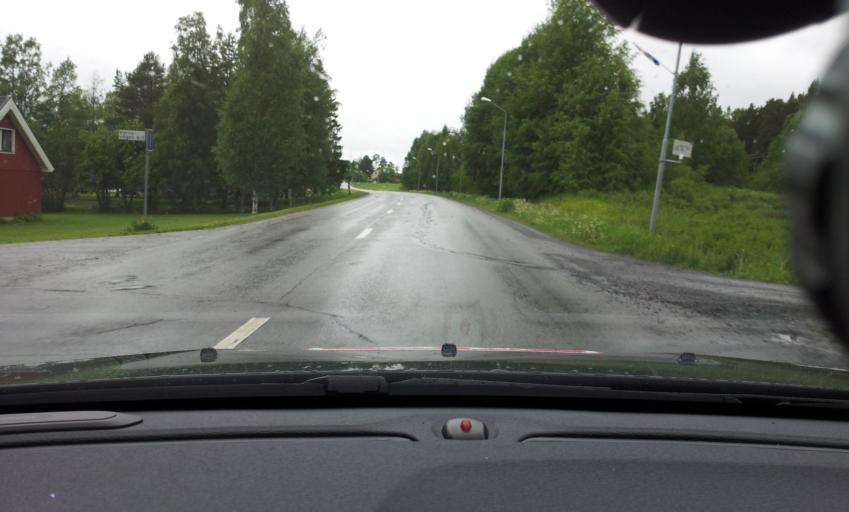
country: SE
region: Jaemtland
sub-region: Krokoms Kommun
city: Krokom
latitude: 63.2983
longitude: 14.4815
